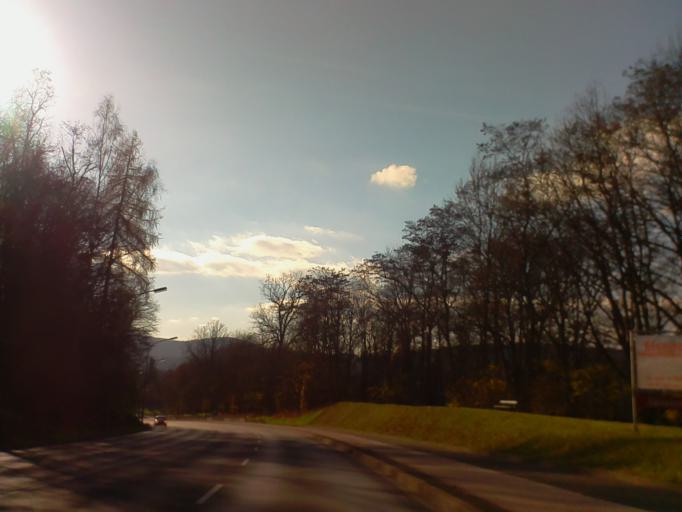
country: DE
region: Bavaria
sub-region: Regierungsbezirk Unterfranken
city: Bad Kissingen
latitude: 50.1914
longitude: 10.0816
